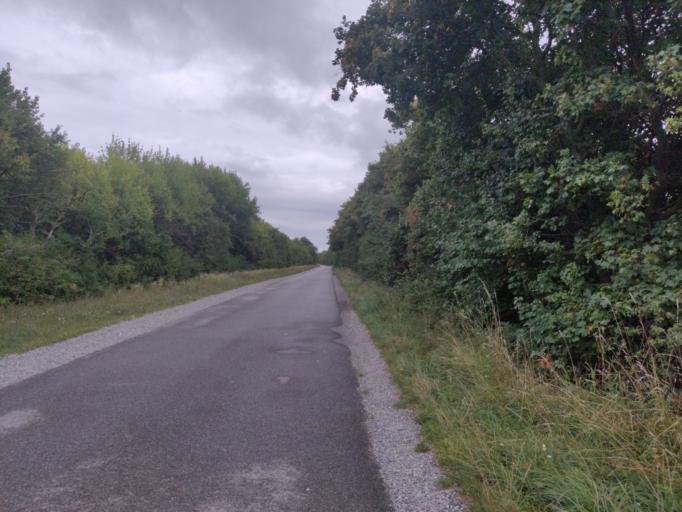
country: AT
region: Lower Austria
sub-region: Politischer Bezirk Korneuburg
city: Langenzersdorf
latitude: 48.2637
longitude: 16.3725
